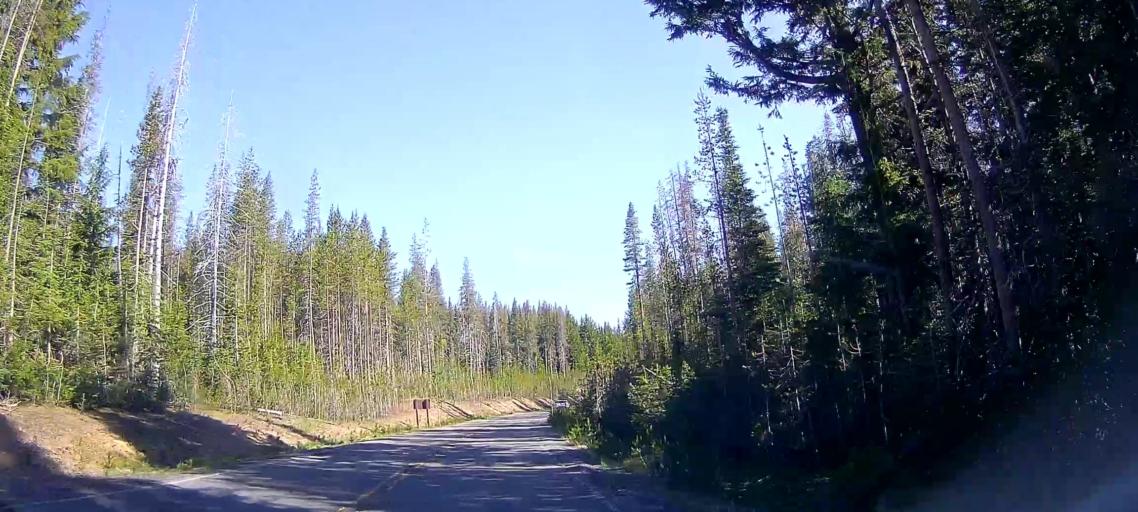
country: US
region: Oregon
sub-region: Jackson County
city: Shady Cove
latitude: 42.8408
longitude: -122.1465
